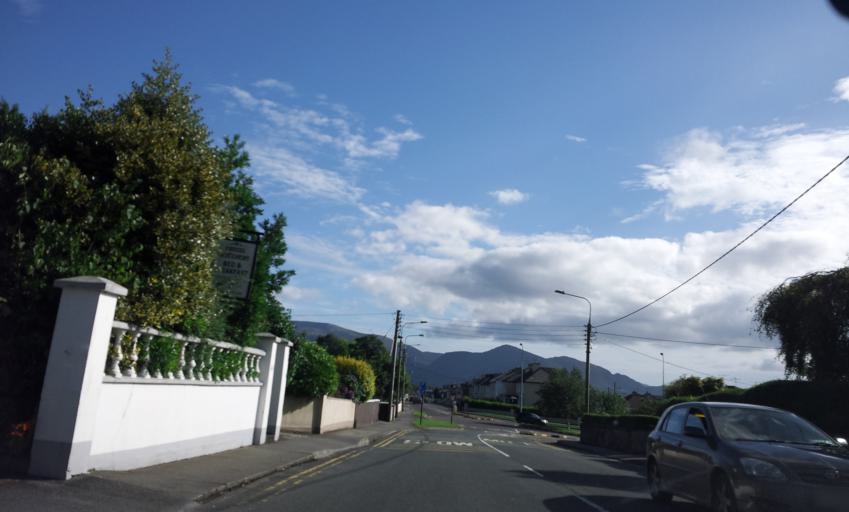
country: IE
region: Munster
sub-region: Ciarrai
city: Cill Airne
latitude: 52.0647
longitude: -9.5061
